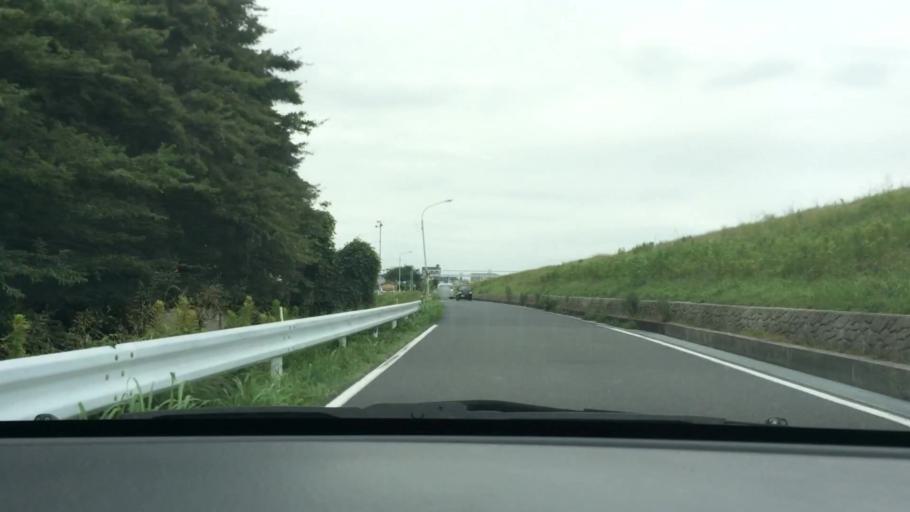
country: JP
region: Chiba
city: Nagareyama
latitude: 35.8322
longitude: 139.8861
